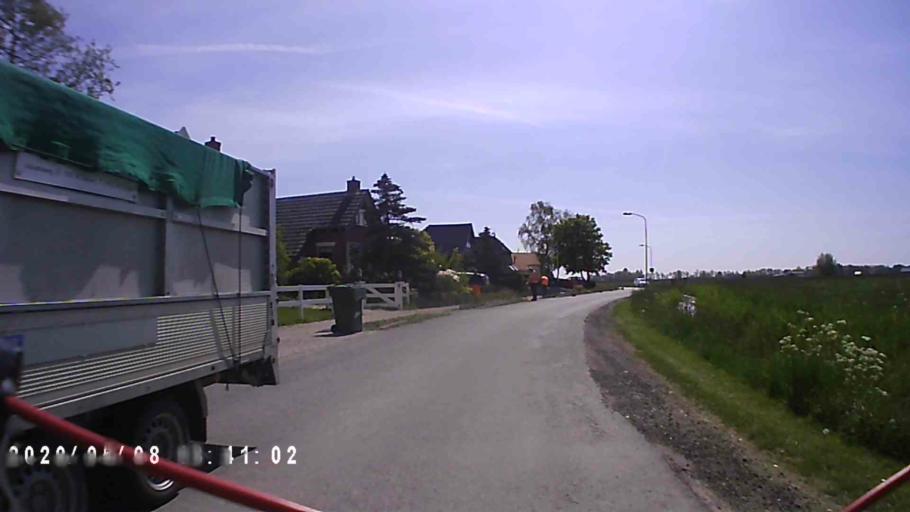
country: NL
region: Groningen
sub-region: Gemeente Appingedam
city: Appingedam
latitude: 53.3226
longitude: 6.7800
